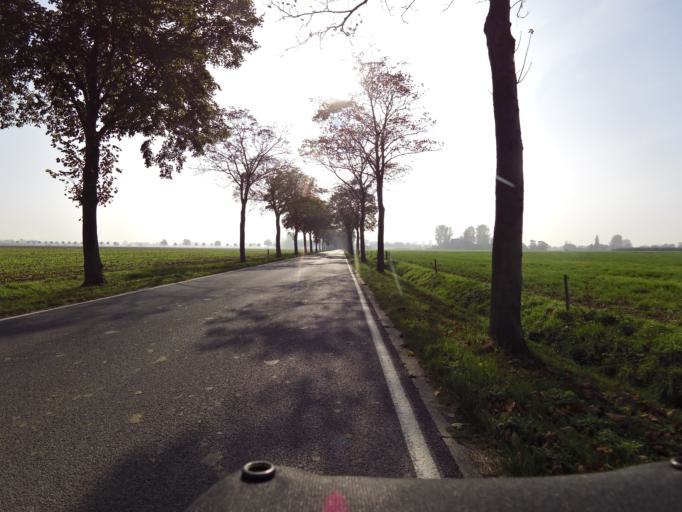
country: DE
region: North Rhine-Westphalia
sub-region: Regierungsbezirk Dusseldorf
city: Kranenburg
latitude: 51.8332
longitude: 6.0328
